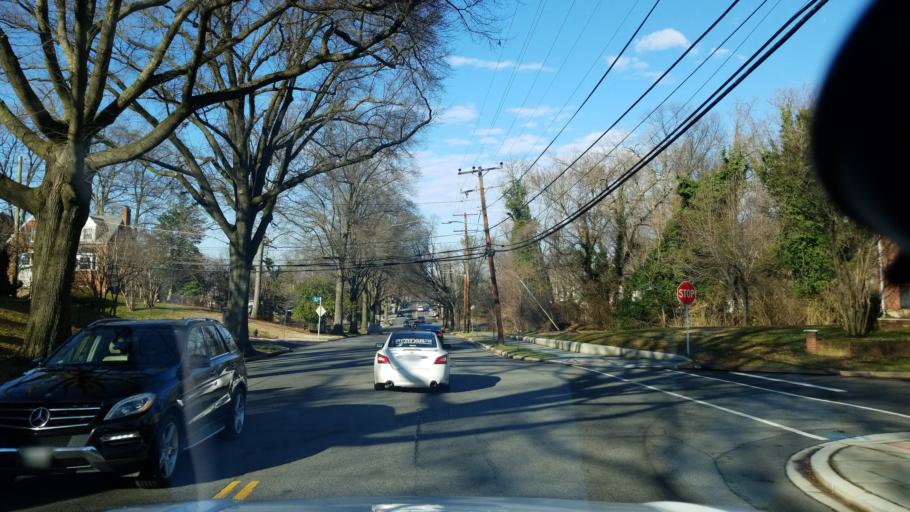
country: US
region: Maryland
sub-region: Prince George's County
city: Silver Hill
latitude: 38.8742
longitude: -76.9610
